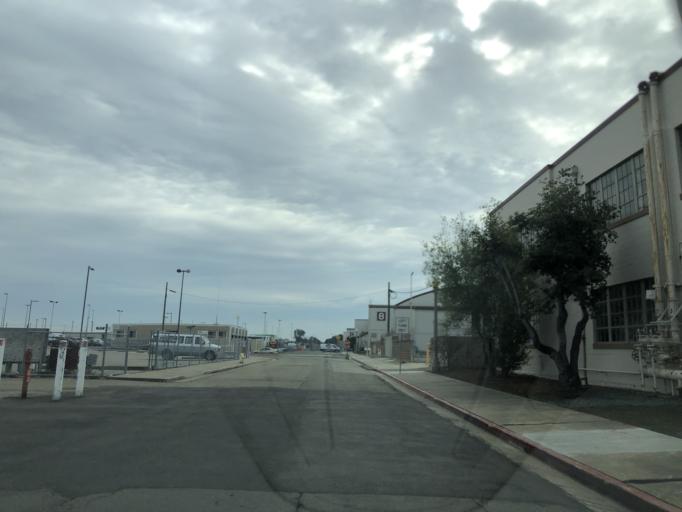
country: US
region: California
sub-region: Alameda County
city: Alameda
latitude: 37.7369
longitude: -122.2172
